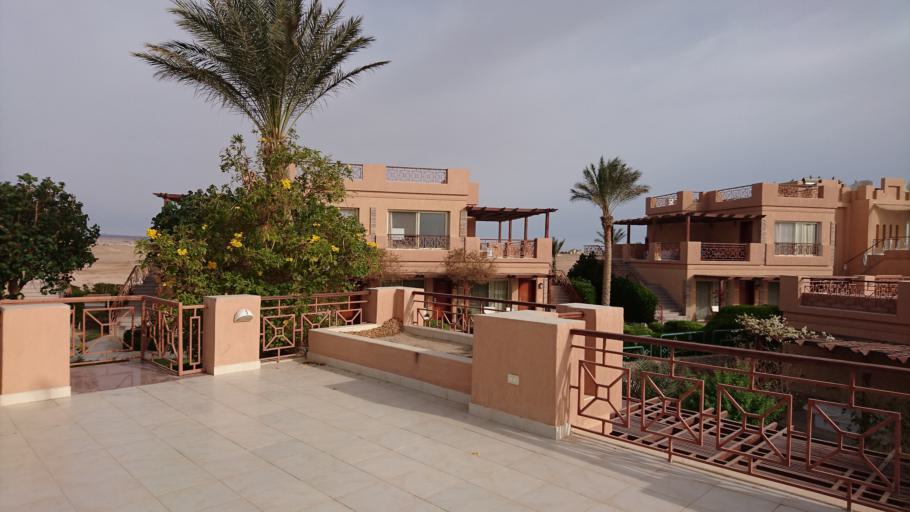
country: EG
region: Red Sea
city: Bur Safajah
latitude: 26.8028
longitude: 33.9457
